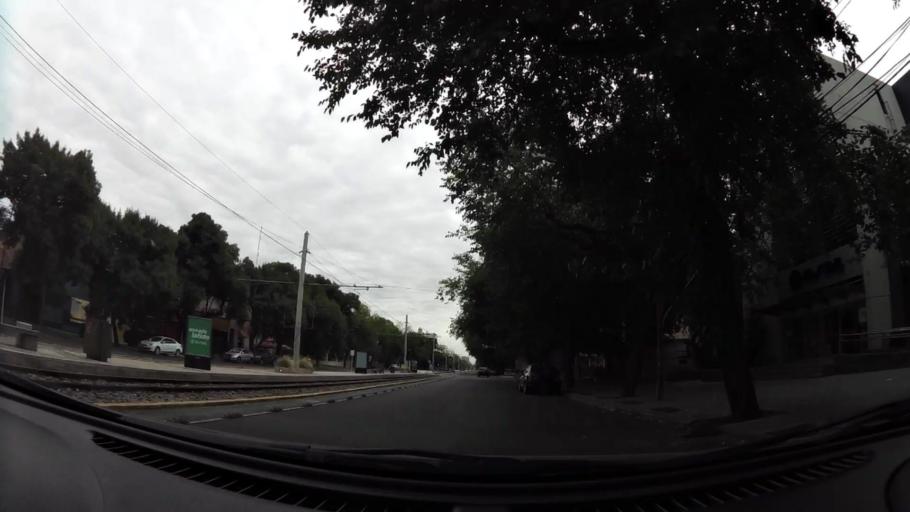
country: AR
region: Mendoza
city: Mendoza
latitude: -32.8915
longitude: -68.8503
